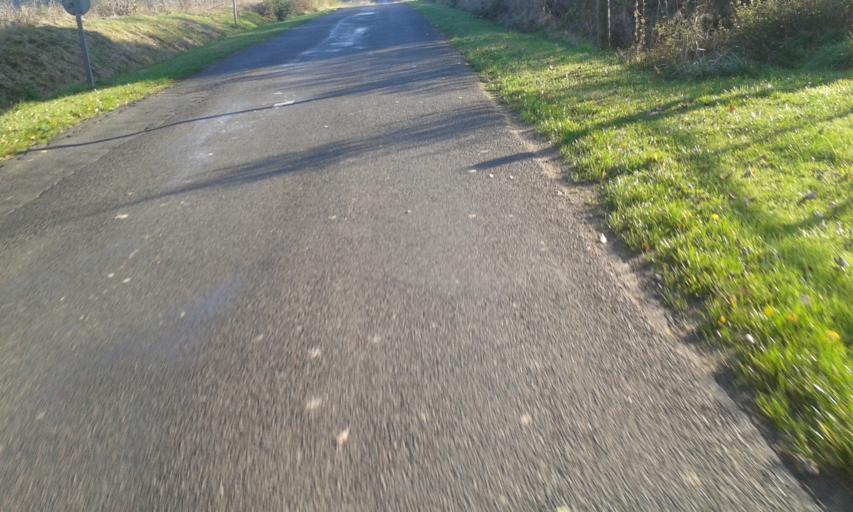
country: FR
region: Centre
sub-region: Departement du Loir-et-Cher
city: Ouzouer-le-Marche
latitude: 47.8644
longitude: 1.4412
